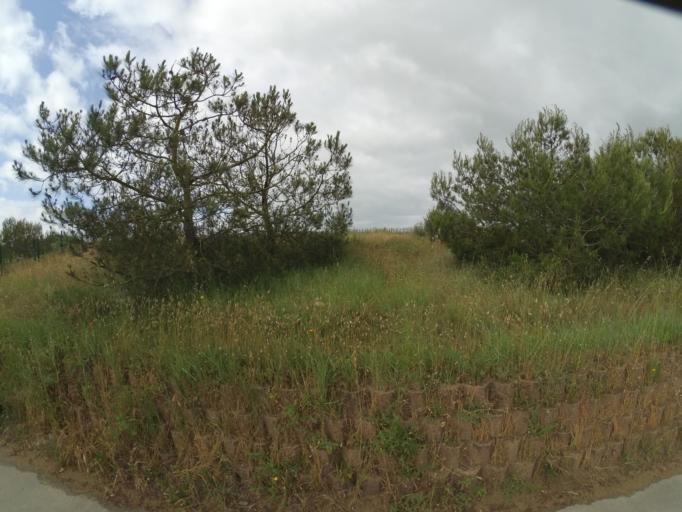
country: FR
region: Poitou-Charentes
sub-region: Departement de la Charente-Maritime
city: Aytre
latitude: 46.1241
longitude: -1.1258
